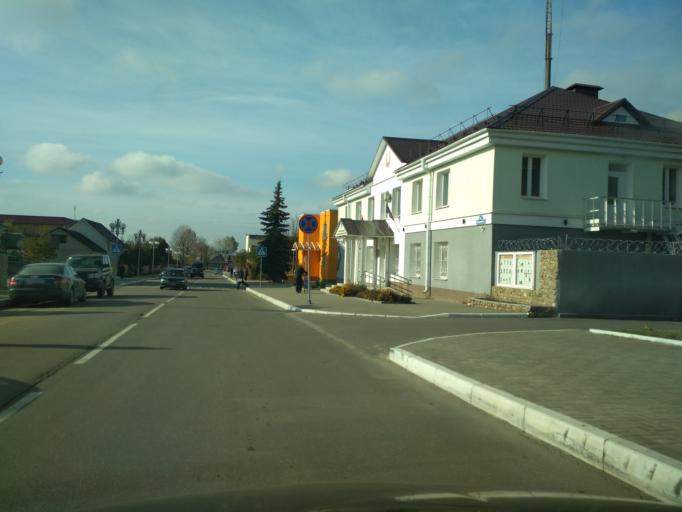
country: BY
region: Minsk
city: Mar''ina Horka
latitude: 53.5105
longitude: 28.1474
